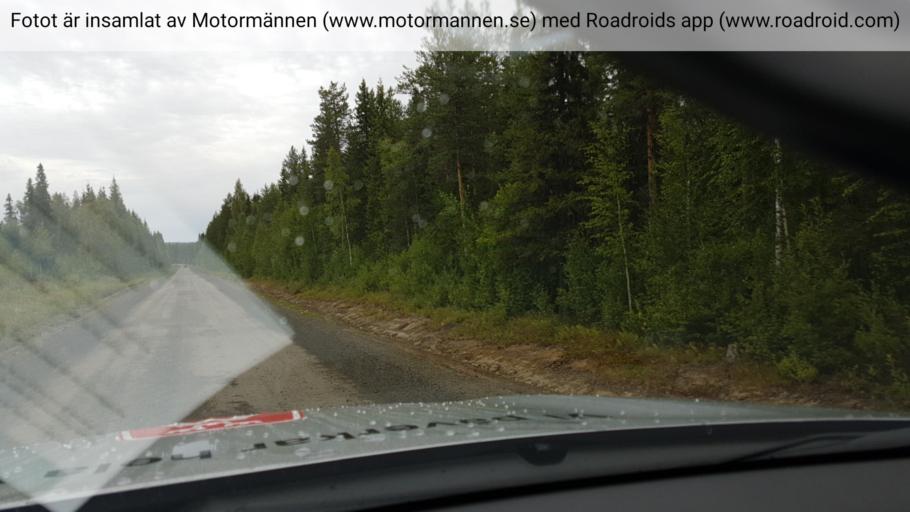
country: SE
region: Norrbotten
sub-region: Alvsbyns Kommun
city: AElvsbyn
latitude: 65.9267
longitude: 21.2570
